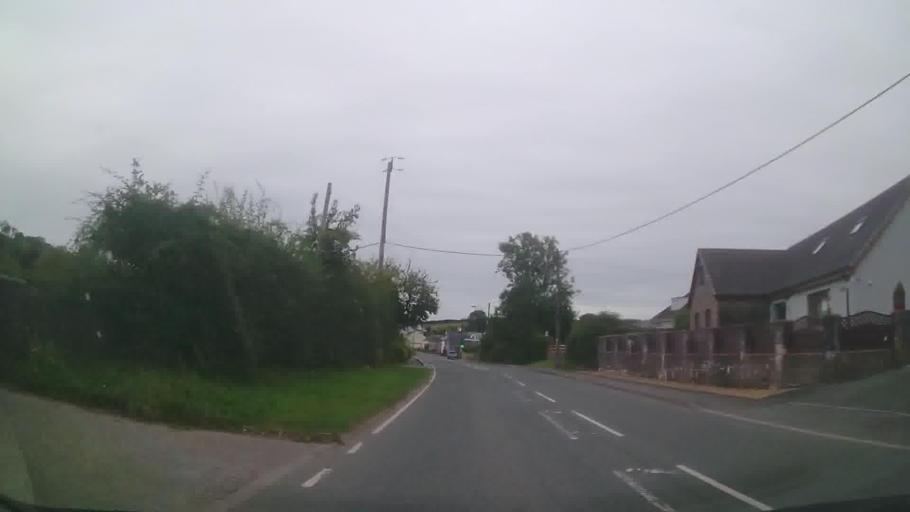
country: GB
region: Wales
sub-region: Carmarthenshire
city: Saint Clears
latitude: 51.7637
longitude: -4.4731
